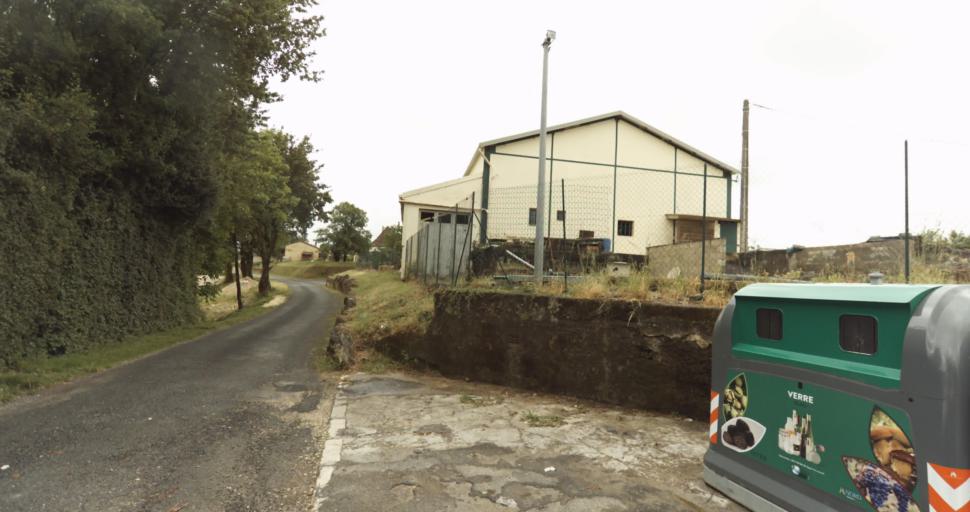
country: FR
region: Aquitaine
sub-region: Departement de la Dordogne
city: Beaumont-du-Perigord
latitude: 44.7595
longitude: 0.7721
